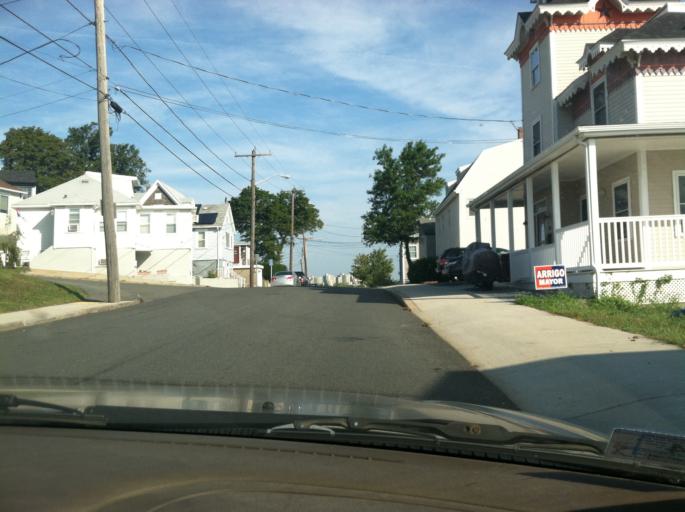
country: US
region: Massachusetts
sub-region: Suffolk County
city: Winthrop
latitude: 42.3942
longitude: -70.9823
